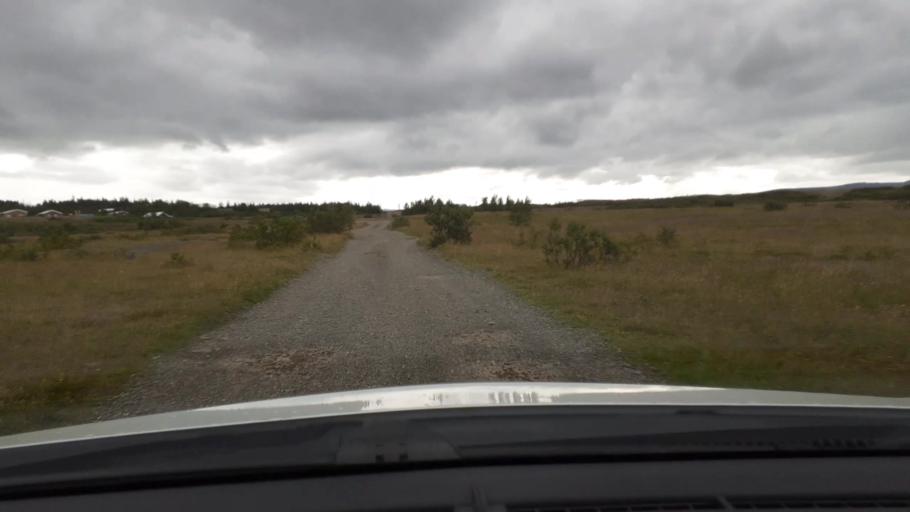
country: IS
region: West
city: Borgarnes
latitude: 64.4619
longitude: -21.9569
